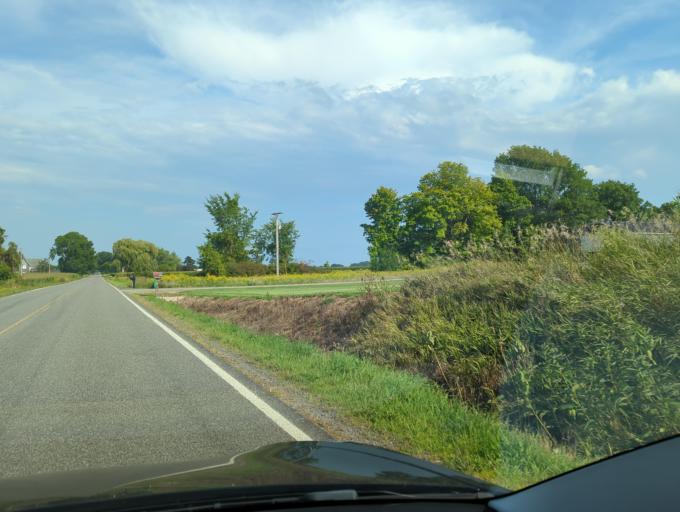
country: US
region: Michigan
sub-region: Ionia County
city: Ionia
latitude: 42.9297
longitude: -85.1057
